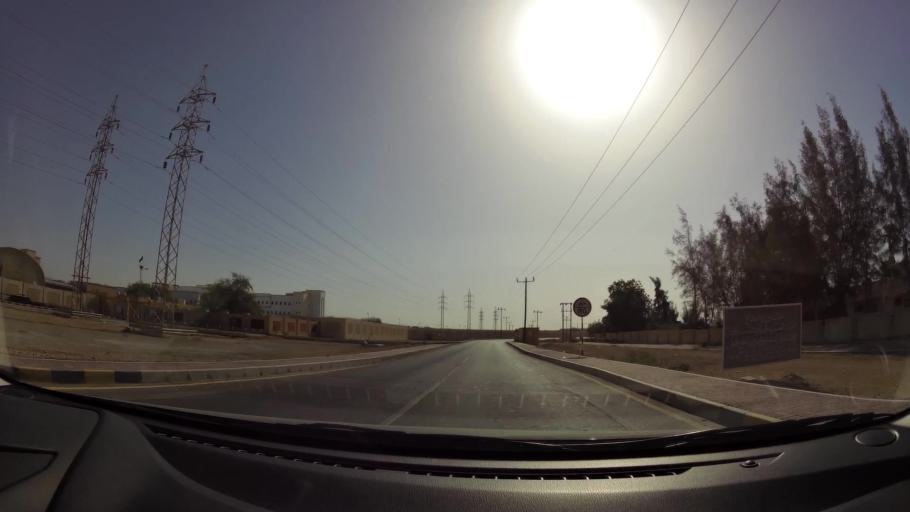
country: OM
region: Muhafazat Masqat
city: As Sib al Jadidah
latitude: 23.5819
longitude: 58.2506
